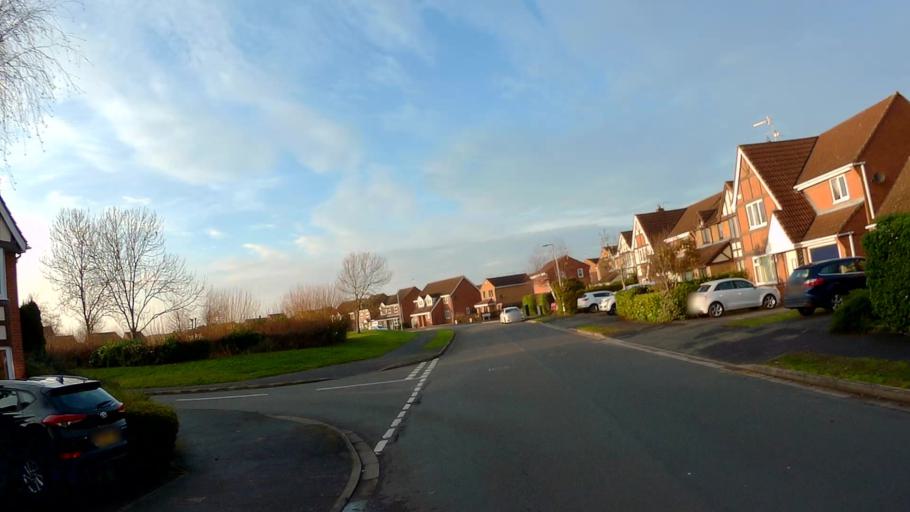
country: GB
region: England
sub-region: Lincolnshire
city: Bourne
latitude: 52.7778
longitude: -0.3787
